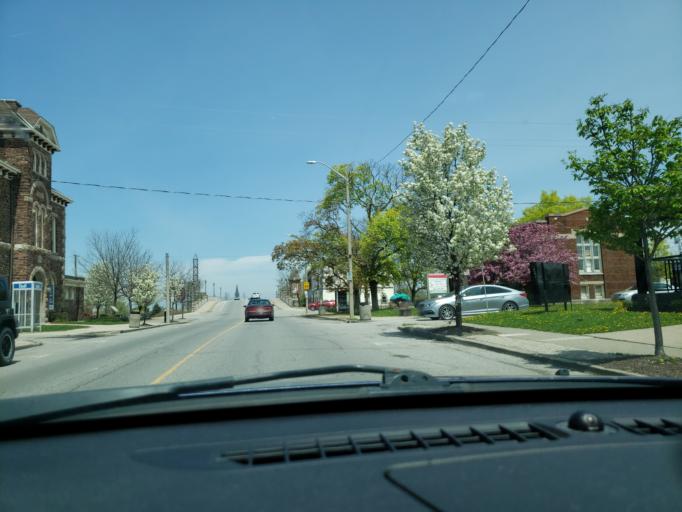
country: CA
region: Ontario
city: Thorold
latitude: 43.1398
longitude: -79.2139
